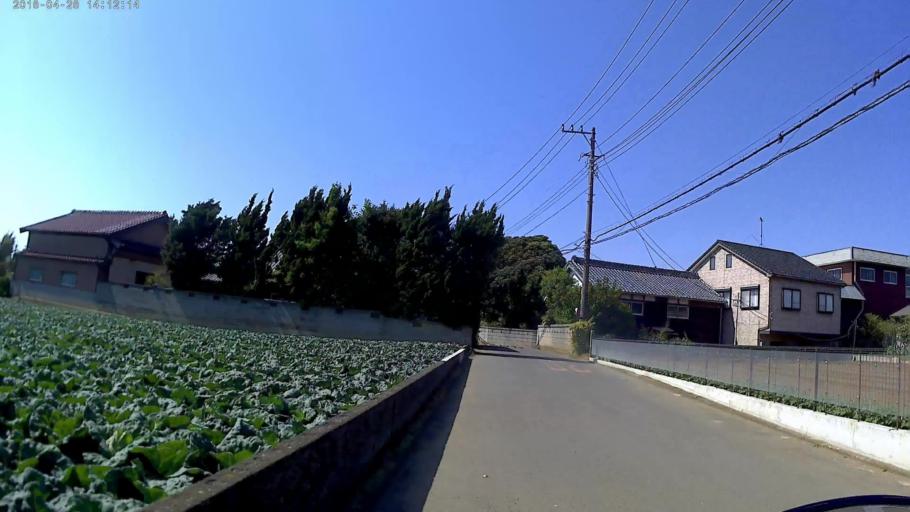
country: JP
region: Kanagawa
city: Miura
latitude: 35.1459
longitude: 139.6519
